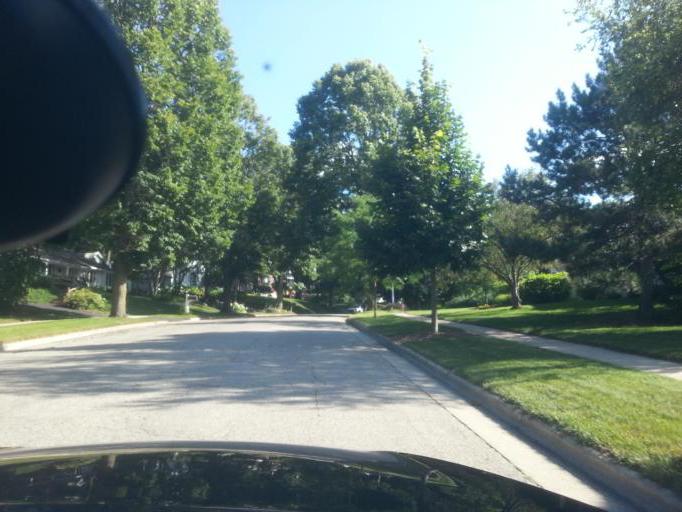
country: US
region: Wisconsin
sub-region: Dane County
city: Middleton
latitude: 43.0747
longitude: -89.4892
